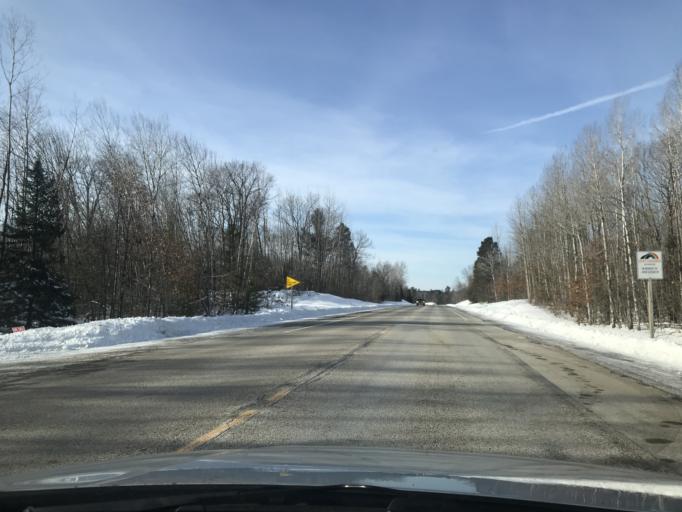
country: US
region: Wisconsin
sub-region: Oconto County
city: Gillett
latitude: 45.1229
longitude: -88.3947
